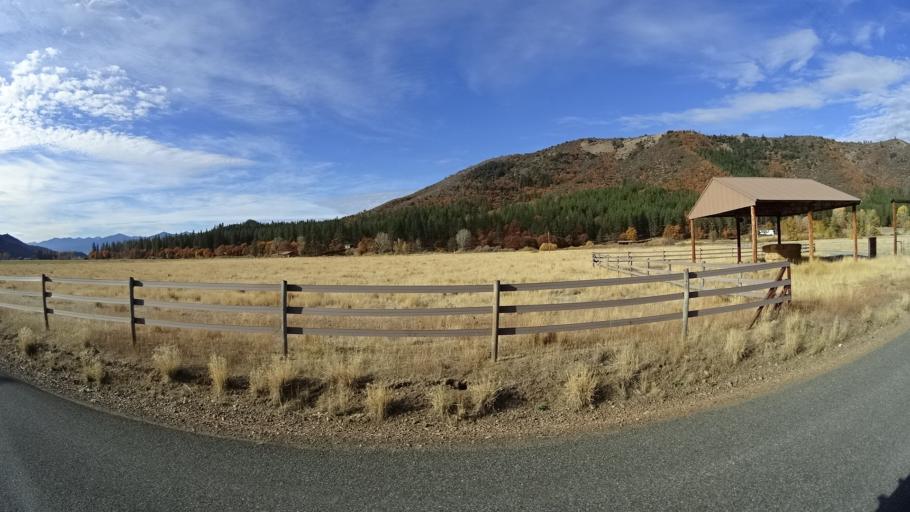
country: US
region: California
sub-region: Siskiyou County
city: Yreka
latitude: 41.6451
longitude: -122.8293
